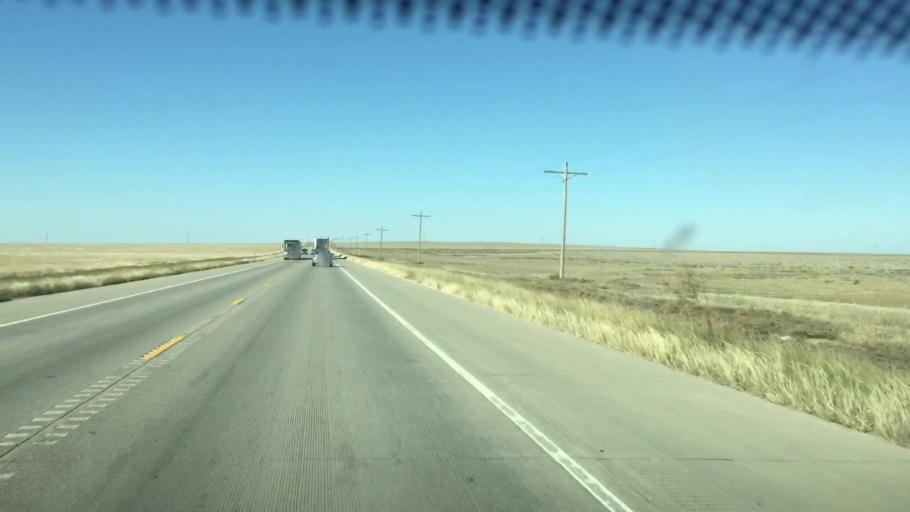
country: US
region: Colorado
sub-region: Prowers County
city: Lamar
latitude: 38.2461
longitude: -102.7240
